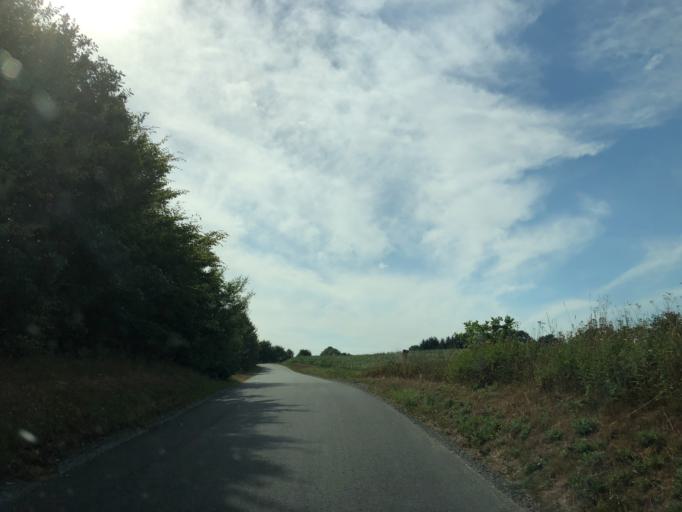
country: DK
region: South Denmark
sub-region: Vejle Kommune
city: Egtved
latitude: 55.6726
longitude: 9.2789
